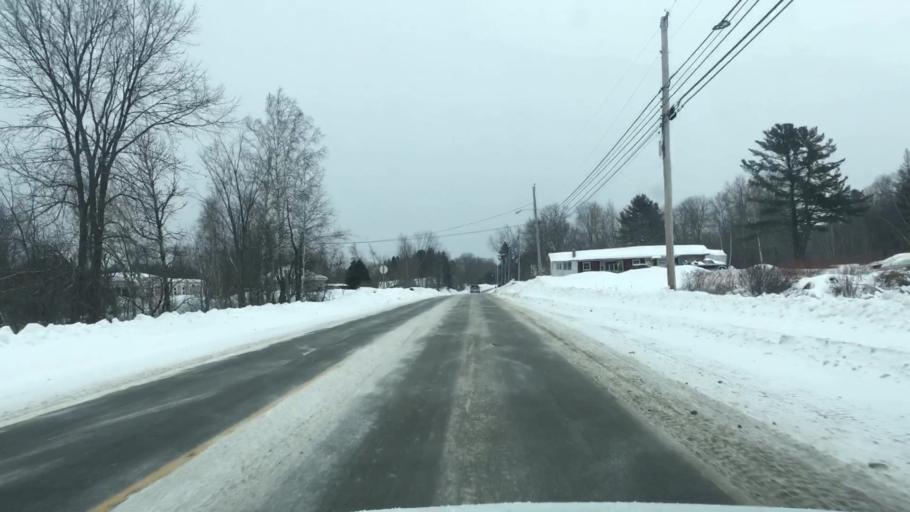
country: US
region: Maine
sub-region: Penobscot County
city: Lincoln
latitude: 45.3981
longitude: -68.4919
